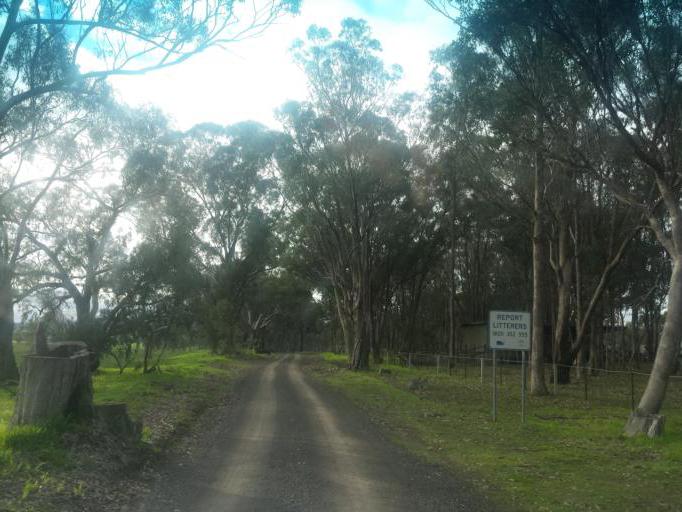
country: AU
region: Victoria
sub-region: Murrindindi
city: Kinglake West
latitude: -37.0491
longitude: 145.2502
